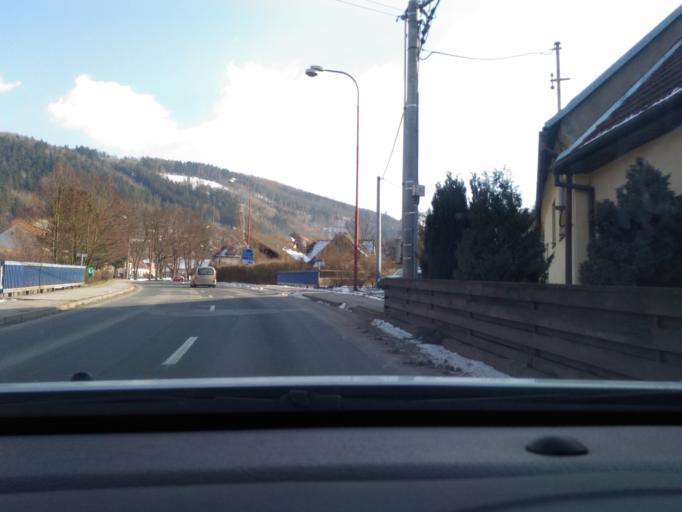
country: CZ
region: South Moravian
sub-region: Okres Brno-Venkov
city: Nedvedice
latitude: 49.4260
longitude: 16.3500
